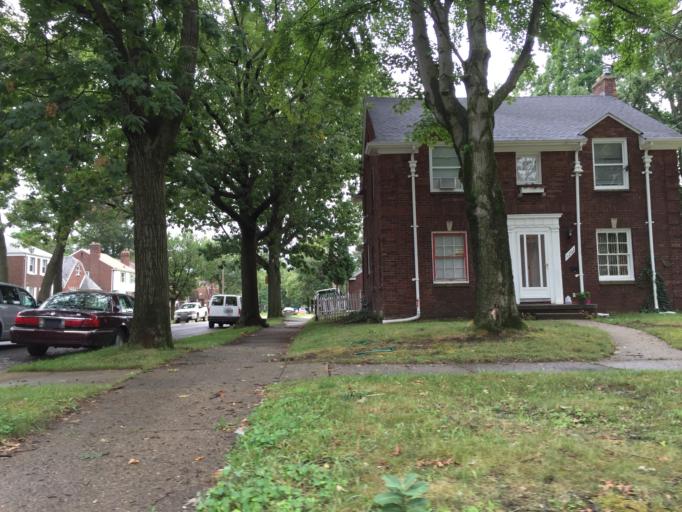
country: US
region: Michigan
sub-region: Oakland County
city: Ferndale
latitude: 42.4139
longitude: -83.1512
